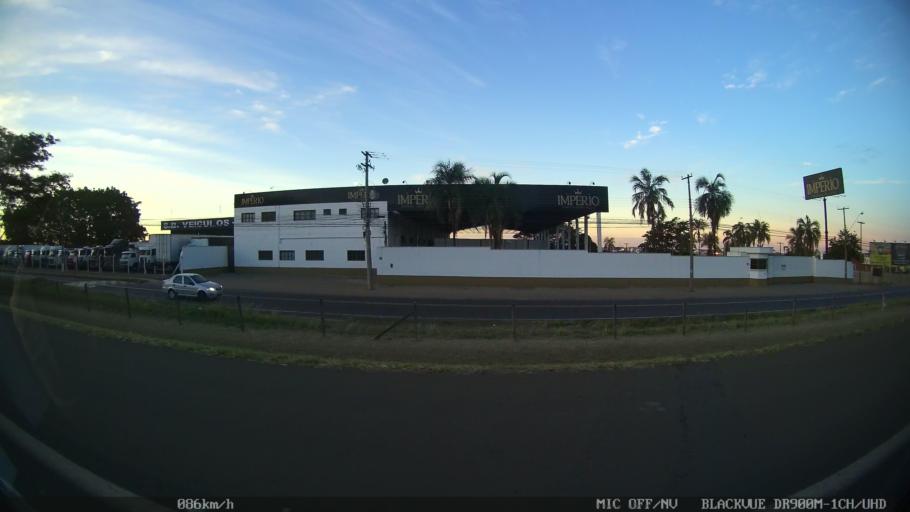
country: BR
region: Sao Paulo
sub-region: Catanduva
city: Catanduva
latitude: -21.1524
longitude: -48.9957
